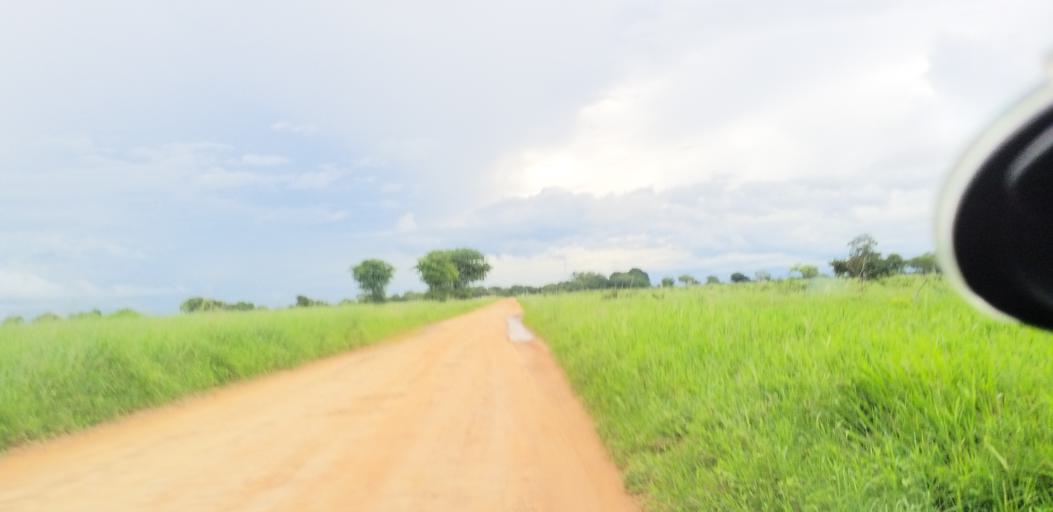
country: ZM
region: Lusaka
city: Chongwe
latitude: -15.1585
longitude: 28.4912
